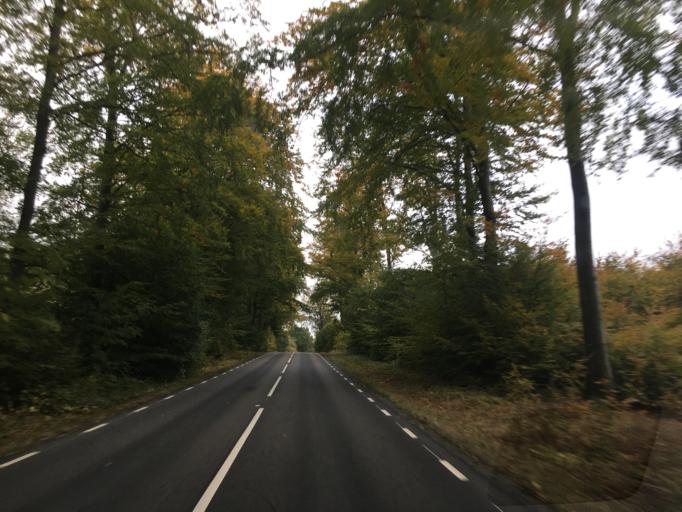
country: SE
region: Skane
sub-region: Simrishamns Kommun
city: Kivik
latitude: 55.6333
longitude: 14.1082
